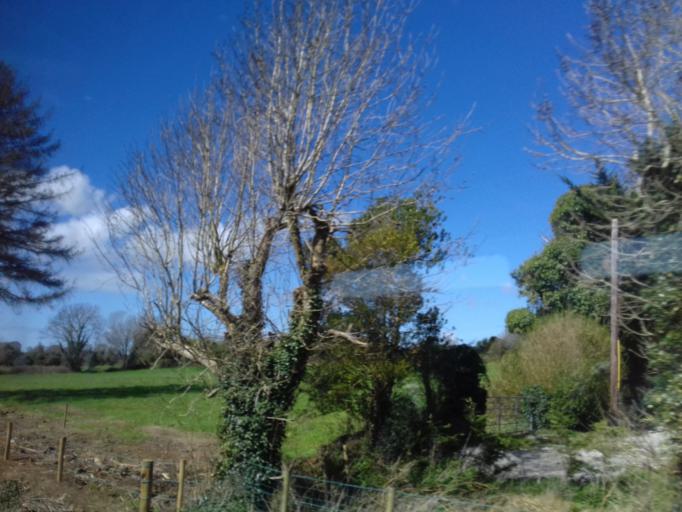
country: IE
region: Munster
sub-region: Ciarrai
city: Tralee
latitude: 52.2396
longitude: -9.6049
